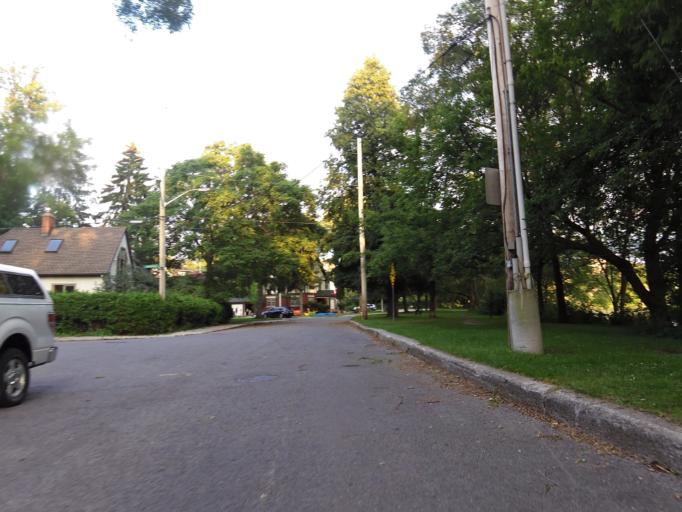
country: CA
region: Ontario
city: Ottawa
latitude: 45.3893
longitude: -75.6817
